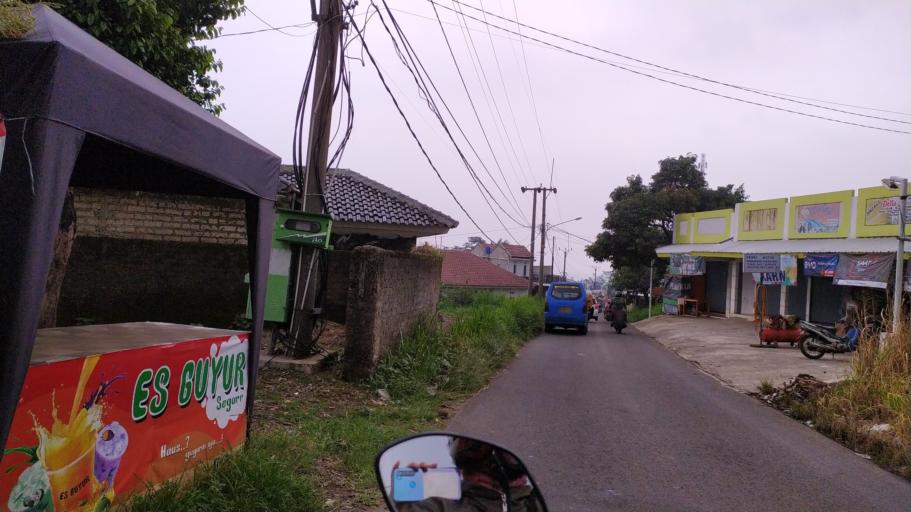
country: ID
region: West Java
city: Ciampea
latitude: -6.6066
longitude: 106.6996
